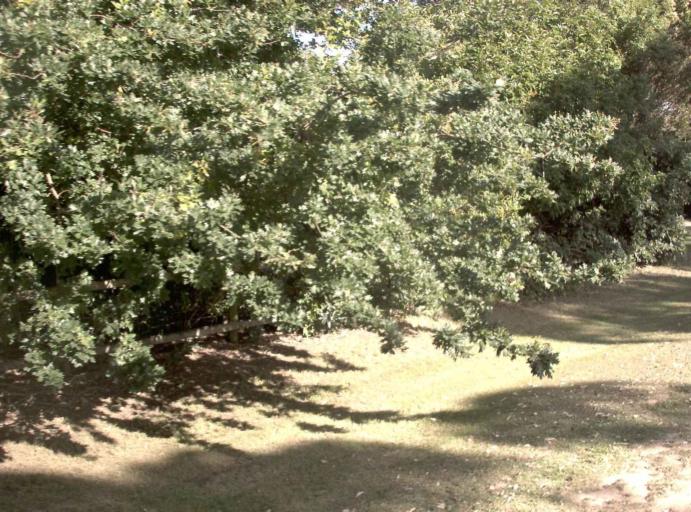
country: AU
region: Victoria
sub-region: East Gippsland
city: Lakes Entrance
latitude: -37.7629
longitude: 148.5388
